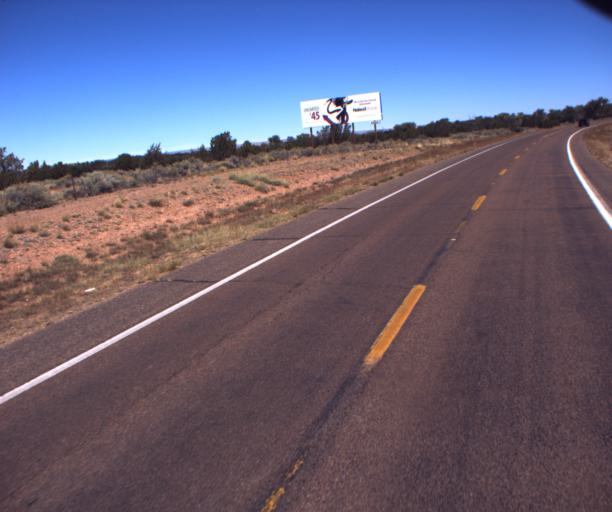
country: US
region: Arizona
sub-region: Apache County
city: Saint Johns
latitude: 34.4845
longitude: -109.3820
